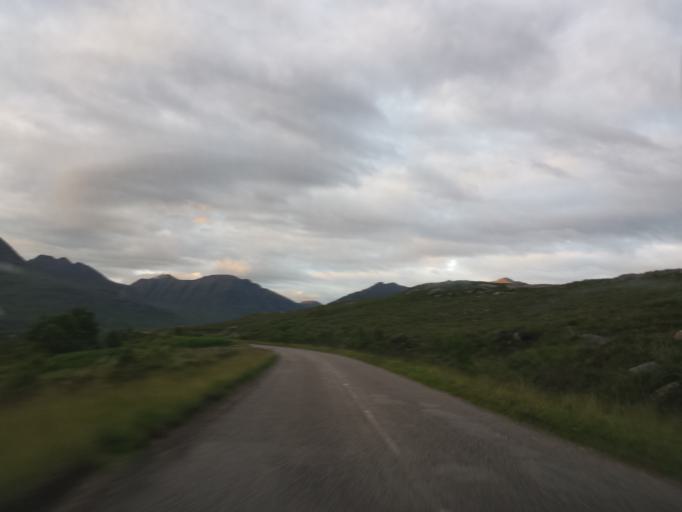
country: GB
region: Scotland
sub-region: Highland
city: Ullapool
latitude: 57.5293
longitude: -5.6111
